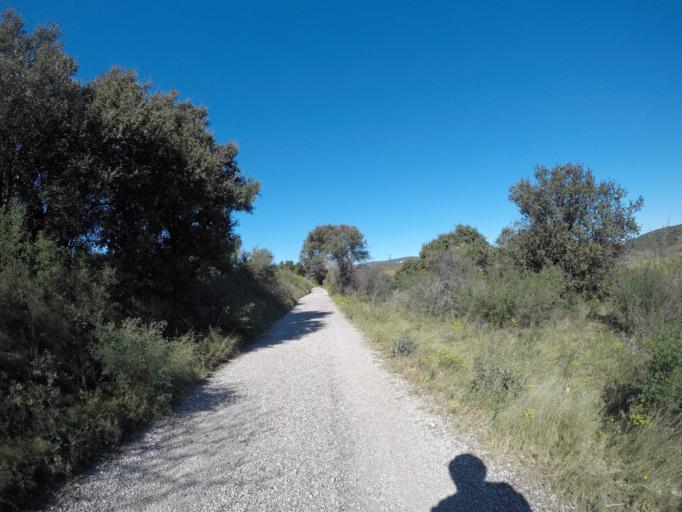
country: FR
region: Languedoc-Roussillon
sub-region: Departement des Pyrenees-Orientales
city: Millas
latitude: 42.7067
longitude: 2.6713
